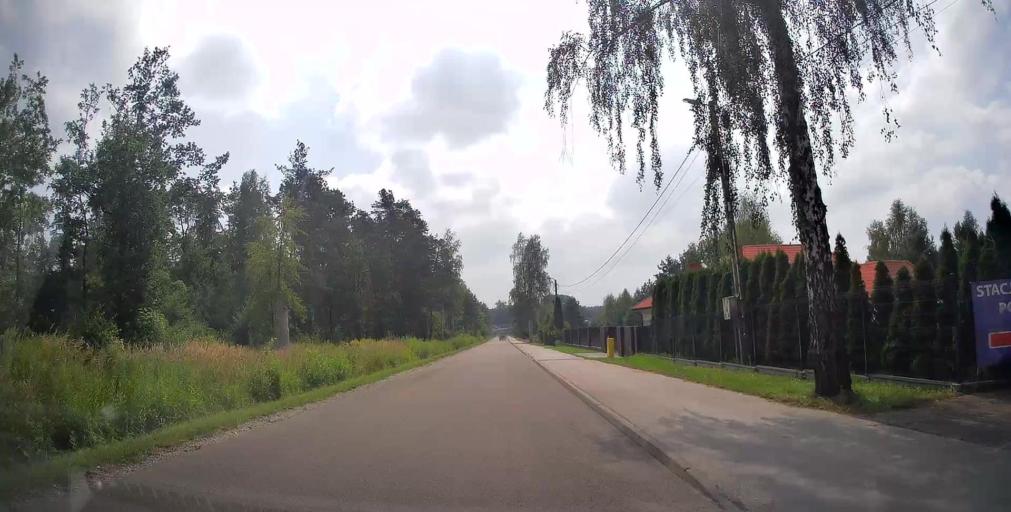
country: PL
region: Masovian Voivodeship
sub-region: Powiat bialobrzeski
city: Sucha
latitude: 51.6265
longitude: 20.9534
